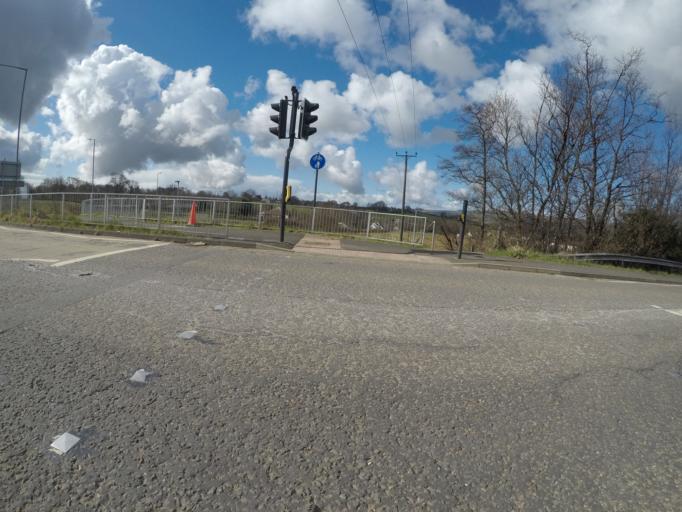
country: GB
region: Scotland
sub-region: North Ayrshire
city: Beith
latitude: 55.7388
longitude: -4.6597
